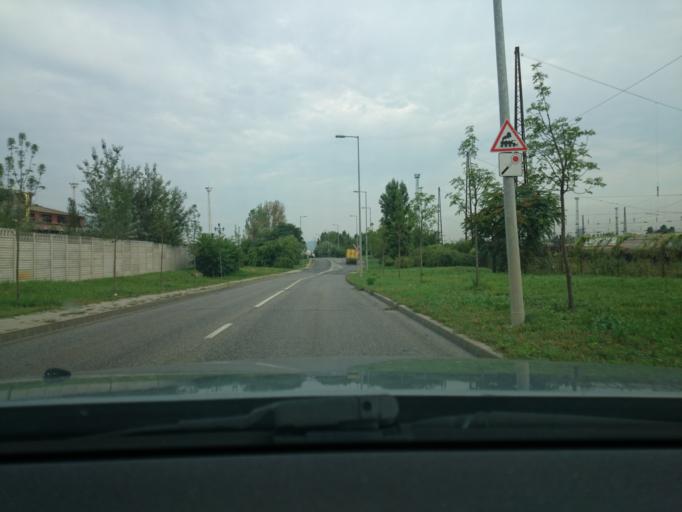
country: HU
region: Budapest
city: Budapest XX. keruelet
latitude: 47.4574
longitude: 19.0955
